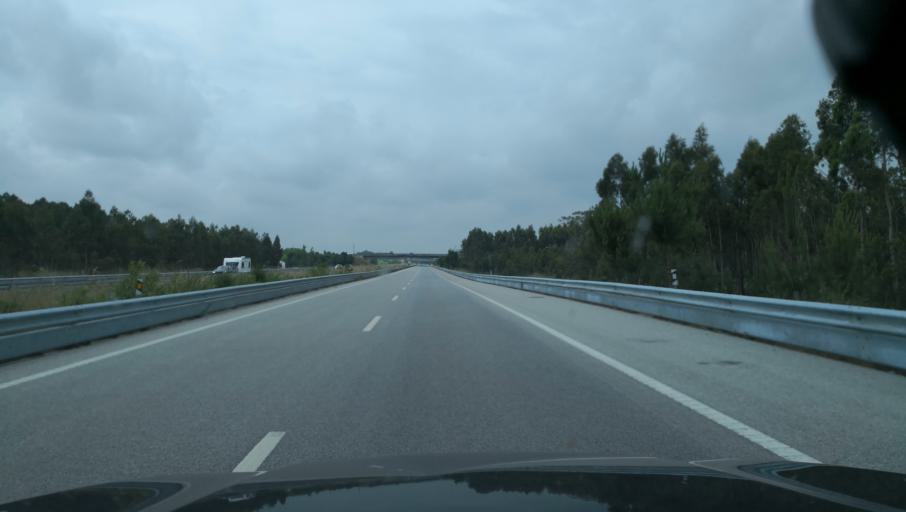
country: PT
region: Coimbra
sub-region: Figueira da Foz
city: Alhadas
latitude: 40.2686
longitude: -8.7599
